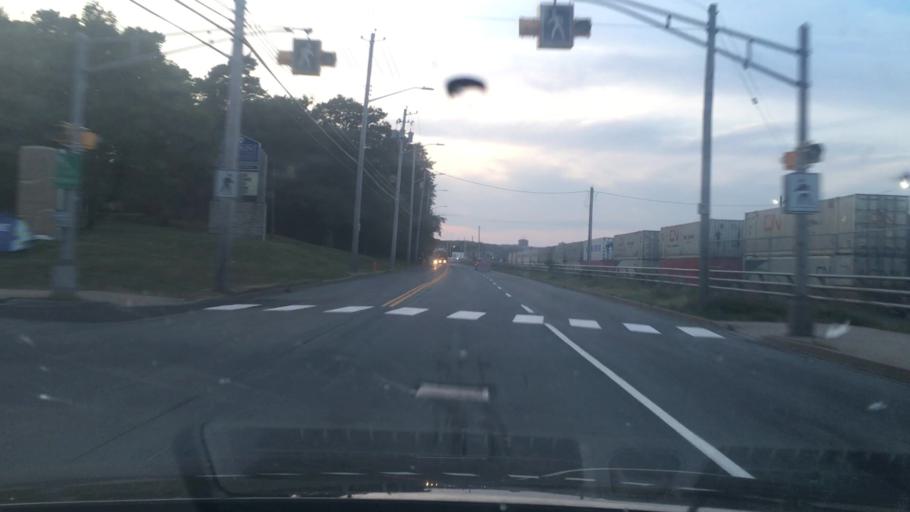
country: CA
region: Nova Scotia
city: Dartmouth
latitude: 44.6705
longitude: -63.6416
